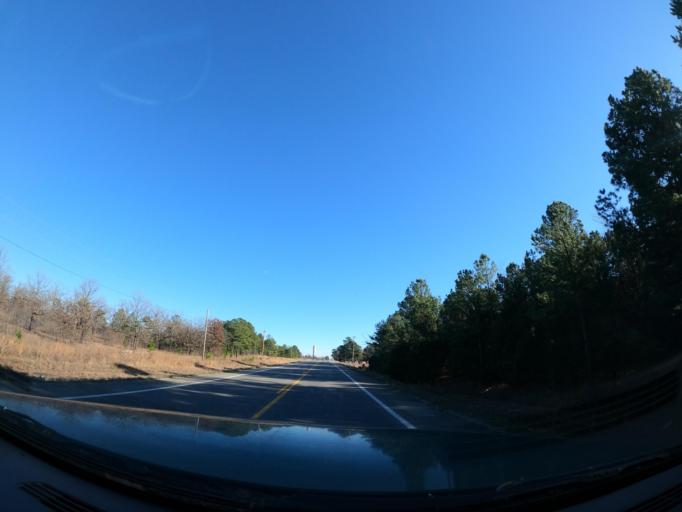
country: US
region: Oklahoma
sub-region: Pittsburg County
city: Longtown
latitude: 35.2315
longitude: -95.4564
